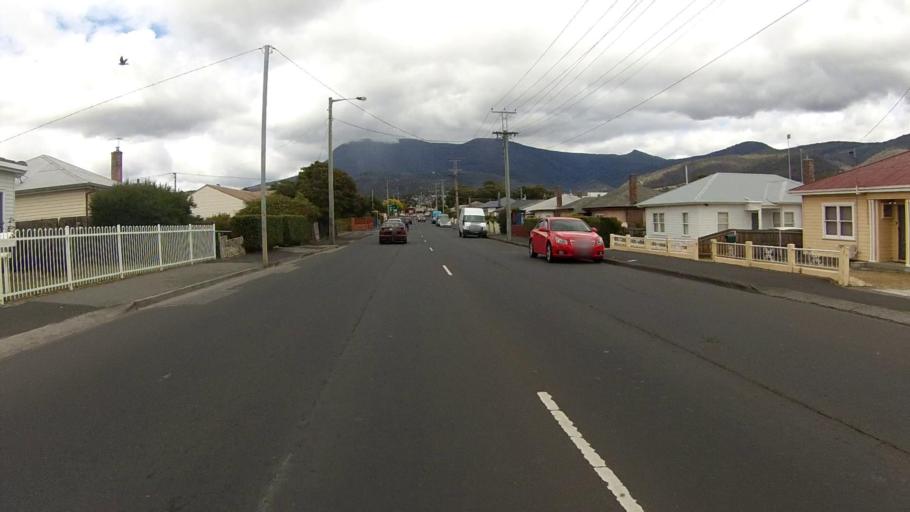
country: AU
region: Tasmania
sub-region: Glenorchy
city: Glenorchy
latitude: -42.8309
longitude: 147.2815
